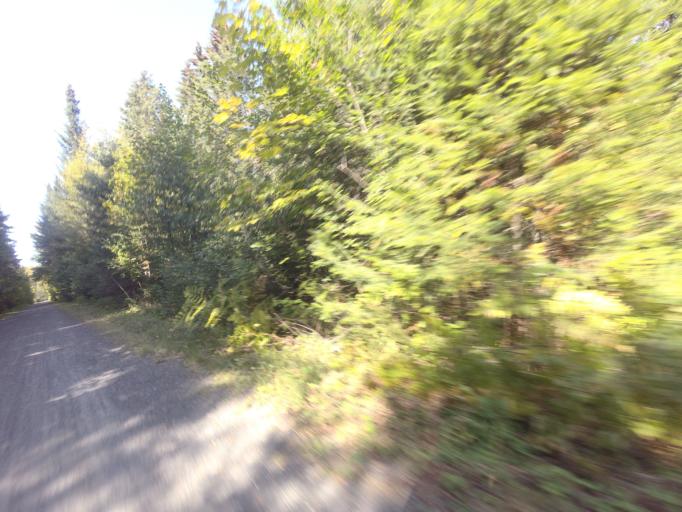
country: CA
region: Quebec
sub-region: Laurentides
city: Sainte-Agathe-des-Monts
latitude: 46.0611
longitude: -74.2968
